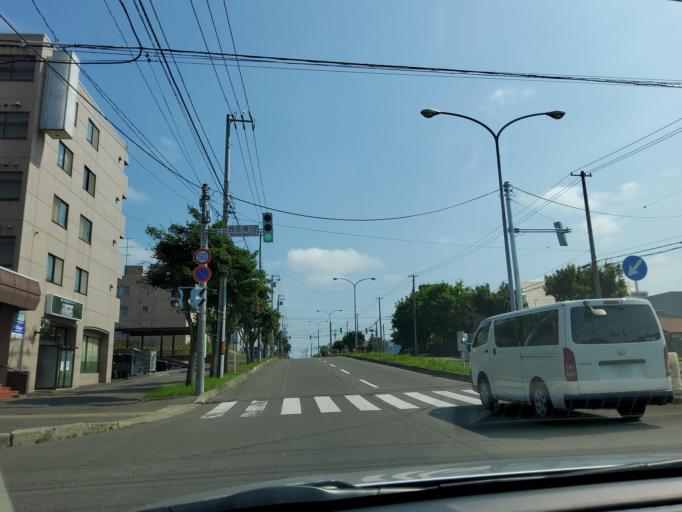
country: JP
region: Hokkaido
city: Obihiro
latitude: 42.9184
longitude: 143.1931
